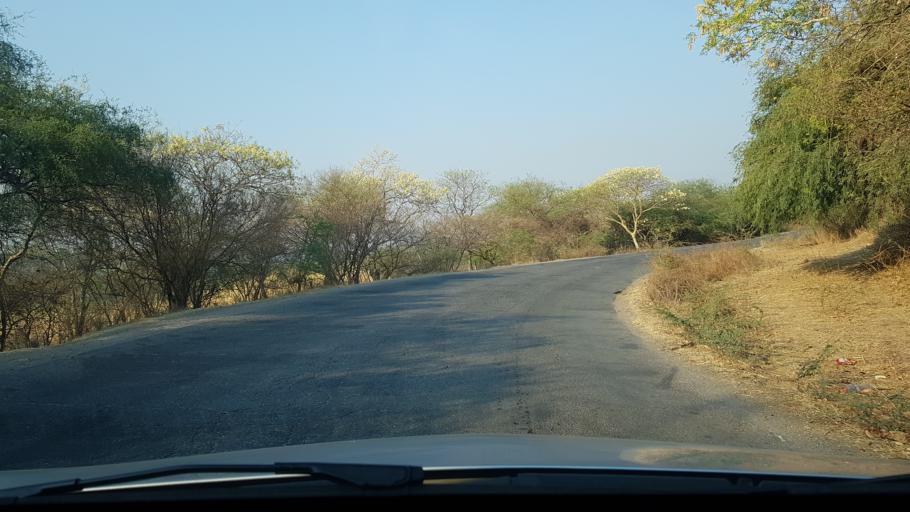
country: MX
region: Morelos
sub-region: Tepalcingo
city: Zacapalco
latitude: 18.6372
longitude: -99.0110
